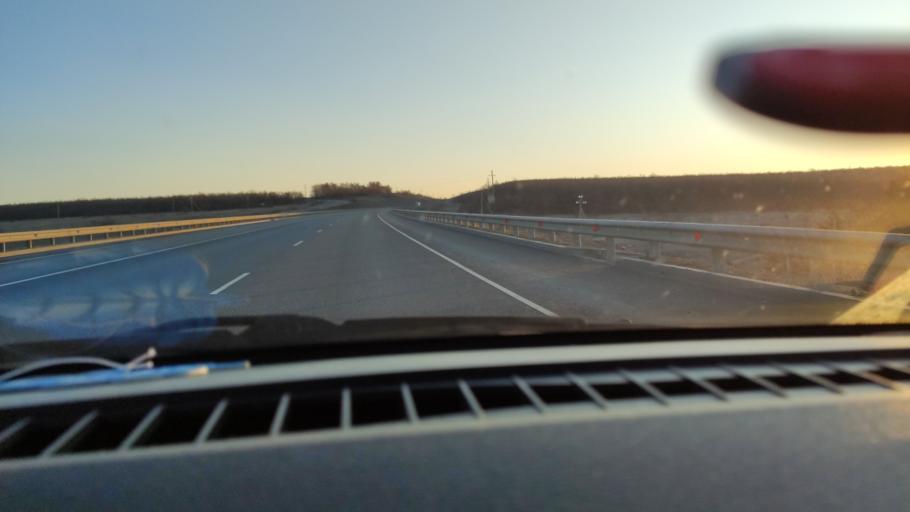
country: RU
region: Saratov
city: Yelshanka
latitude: 51.8803
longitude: 46.5100
